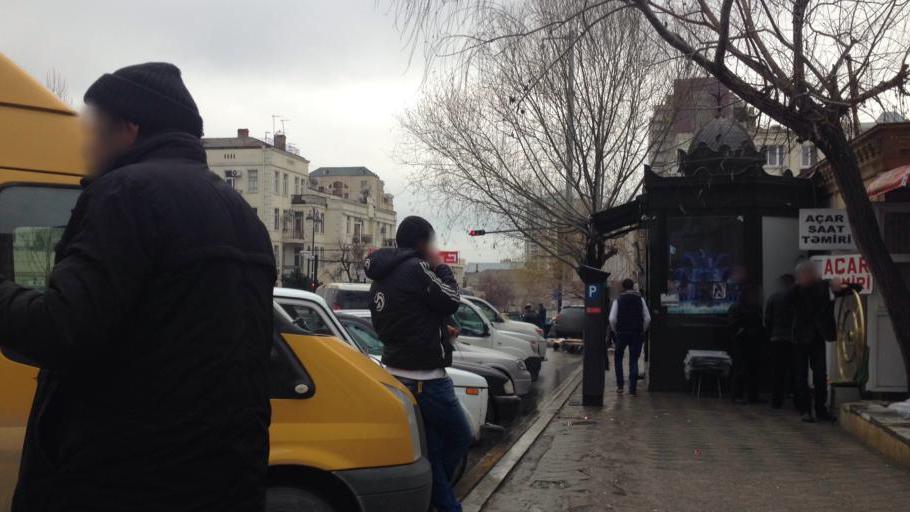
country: AZ
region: Baki
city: Baku
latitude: 40.3813
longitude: 49.8390
